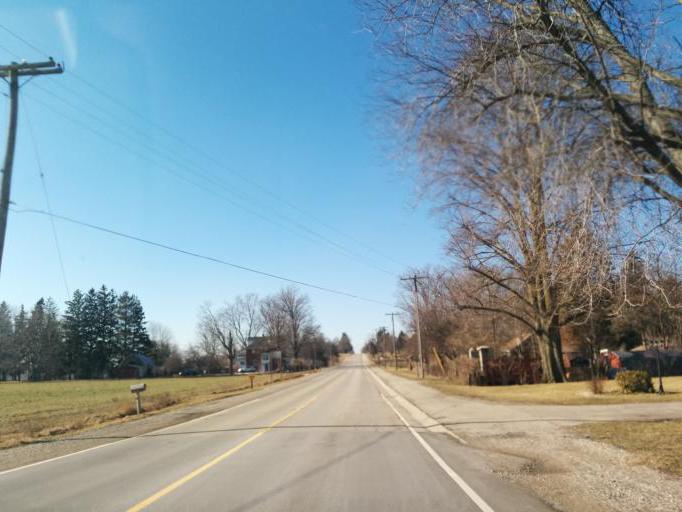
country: CA
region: Ontario
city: Brant
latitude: 43.0333
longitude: -80.3214
